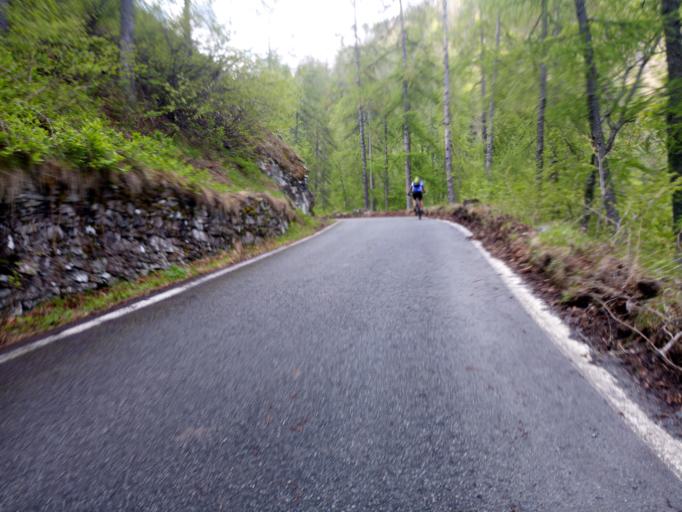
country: IT
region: Piedmont
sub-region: Provincia di Torino
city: Meana di Susa
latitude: 45.1020
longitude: 7.0643
